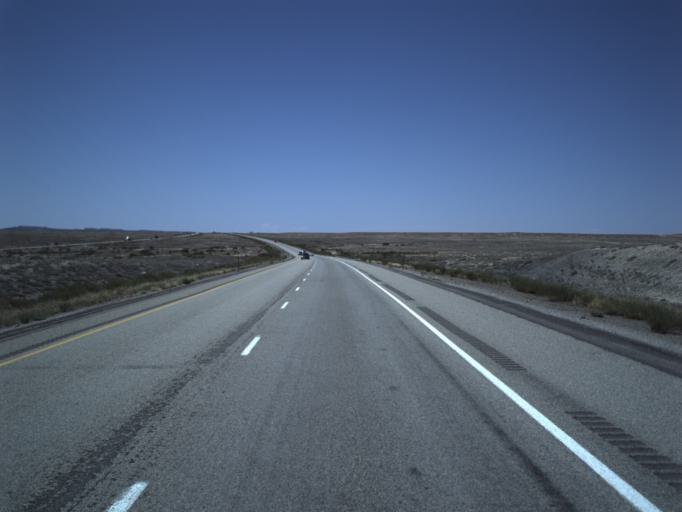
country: US
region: Utah
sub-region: Grand County
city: Moab
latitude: 38.9704
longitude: -109.3660
